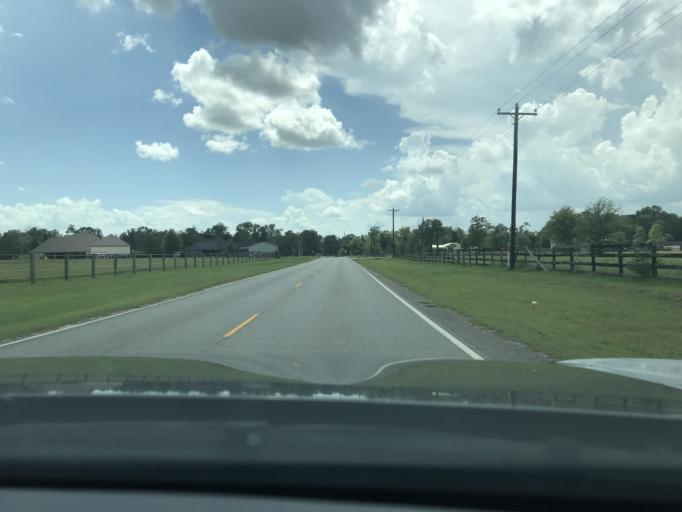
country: US
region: Louisiana
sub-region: Calcasieu Parish
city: Moss Bluff
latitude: 30.3399
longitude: -93.2500
